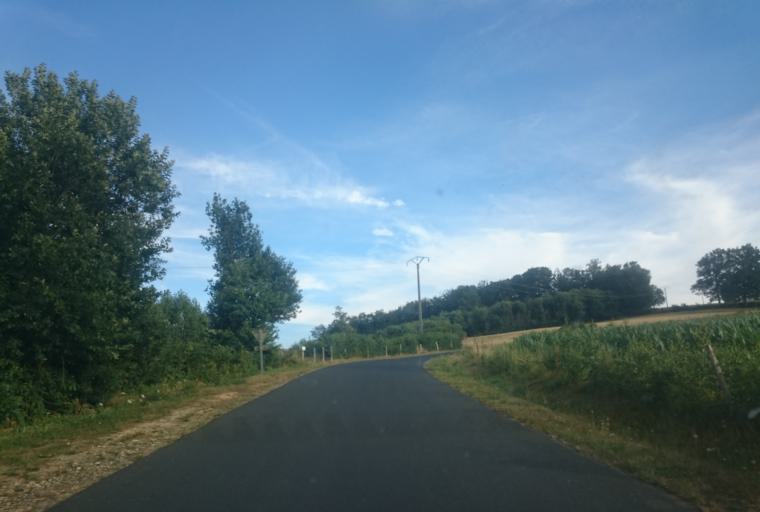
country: FR
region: Auvergne
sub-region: Departement du Cantal
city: Laroquebrou
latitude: 44.9417
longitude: 2.2081
